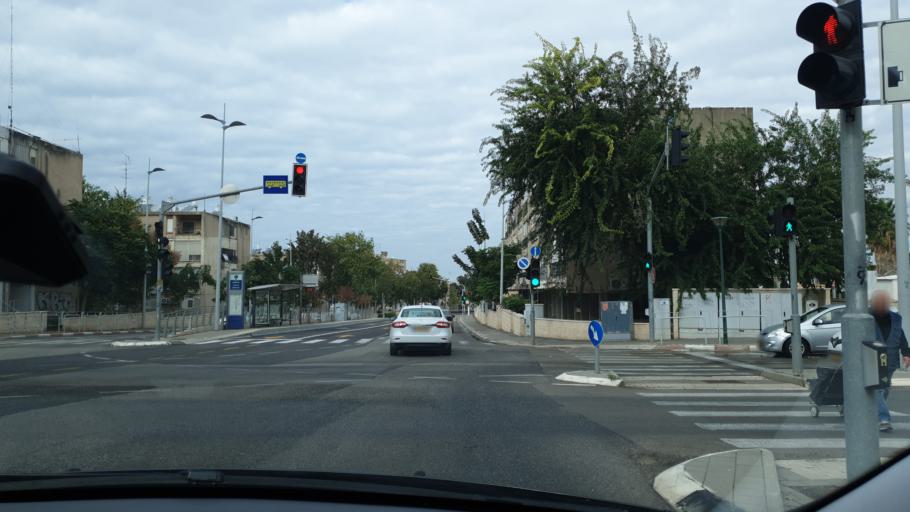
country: IL
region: Haifa
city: Qiryat Ata
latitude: 32.8133
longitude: 35.1144
